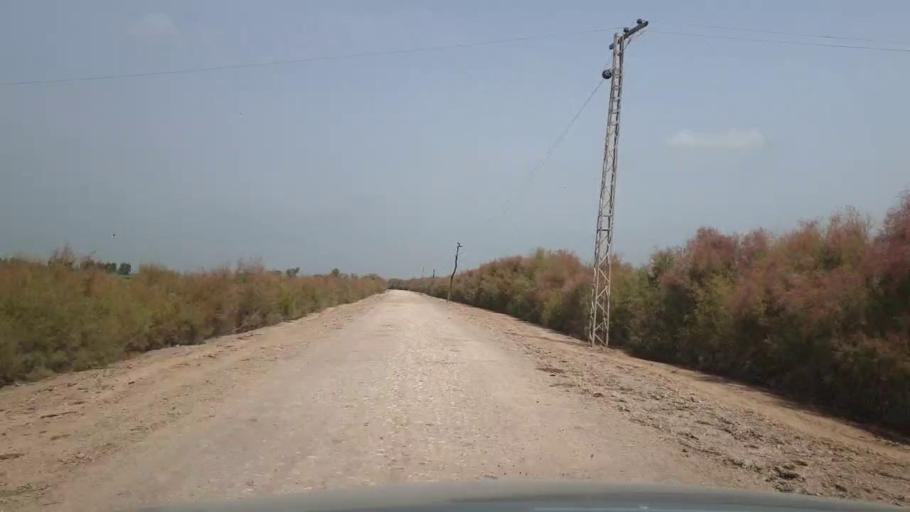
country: PK
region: Sindh
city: Garhi Yasin
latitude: 27.9543
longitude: 68.3657
